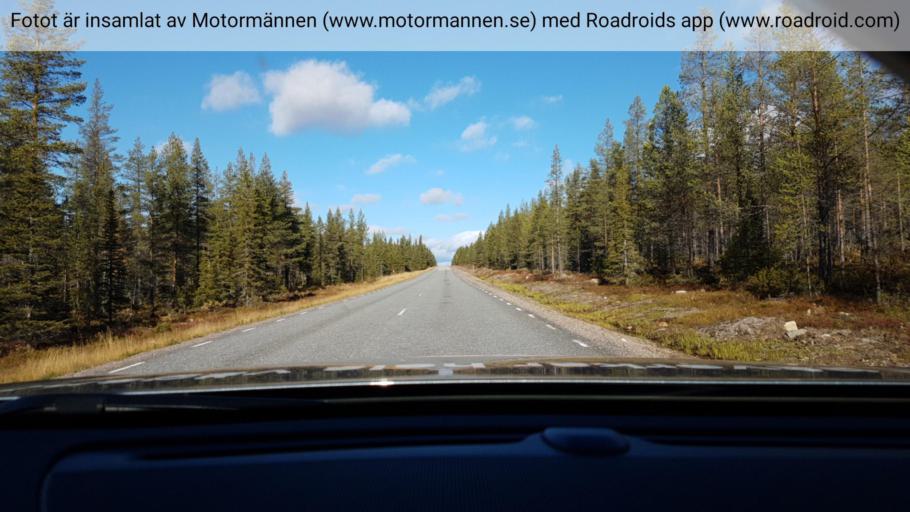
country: SE
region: Norrbotten
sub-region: Arjeplogs Kommun
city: Arjeplog
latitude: 65.8261
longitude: 18.4363
